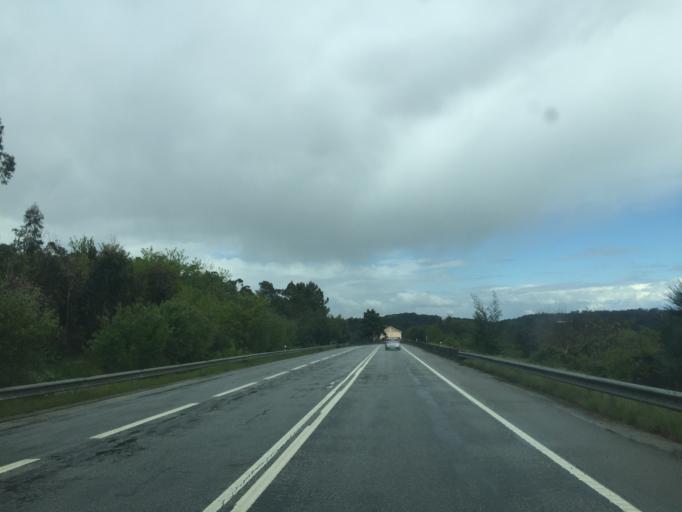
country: PT
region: Viseu
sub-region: Viseu
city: Abraveses
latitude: 40.6600
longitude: -8.0100
